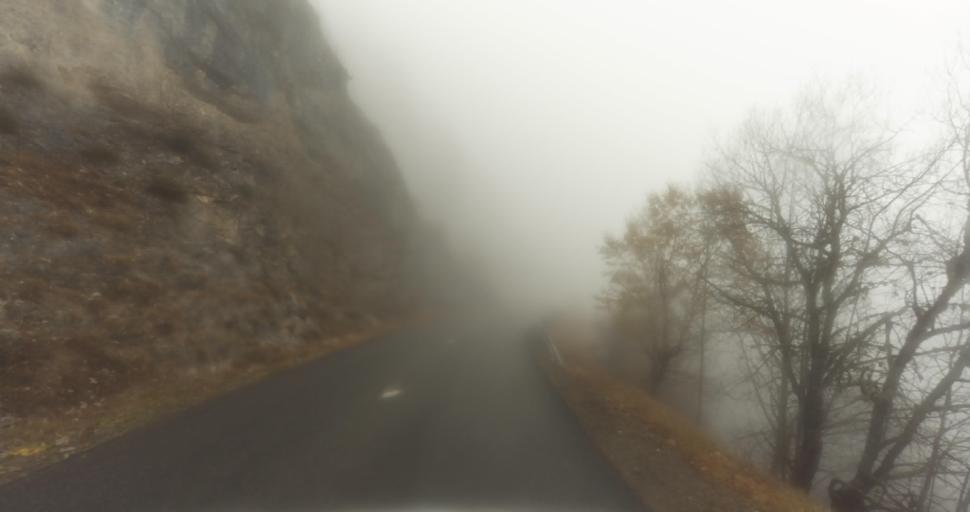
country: FR
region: Rhone-Alpes
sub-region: Departement de la Haute-Savoie
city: Thorens-Glieres
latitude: 45.9576
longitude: 6.3088
